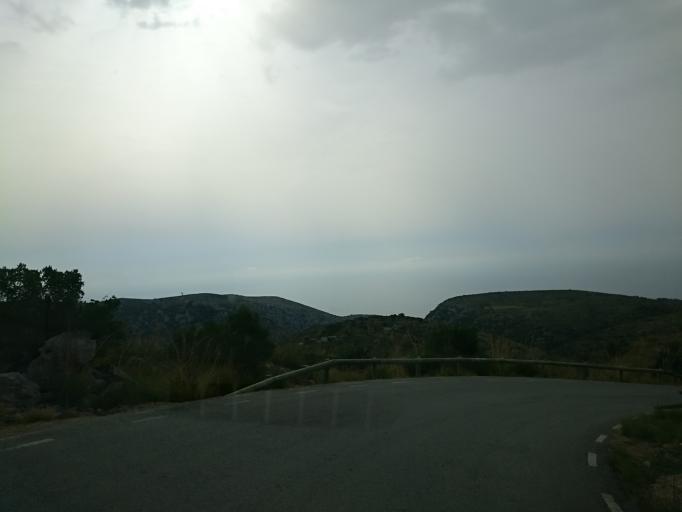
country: ES
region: Catalonia
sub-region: Provincia de Barcelona
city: Begues
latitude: 41.2821
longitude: 1.9129
